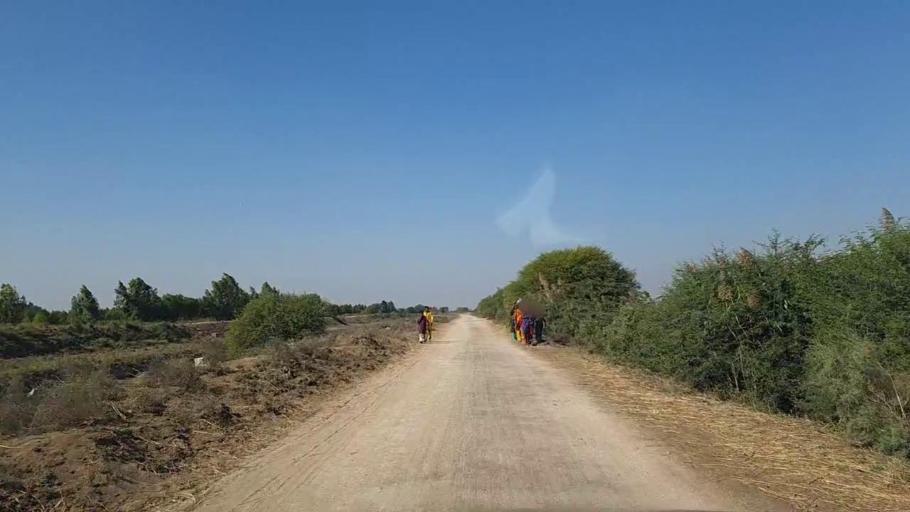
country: PK
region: Sindh
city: Mirpur Batoro
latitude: 24.7274
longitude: 68.2304
